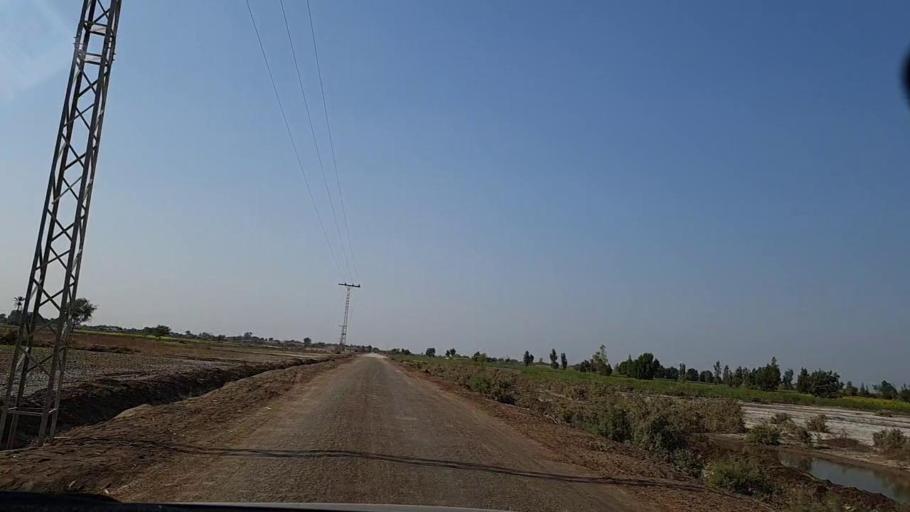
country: PK
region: Sindh
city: Digri
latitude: 25.1721
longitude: 69.0177
